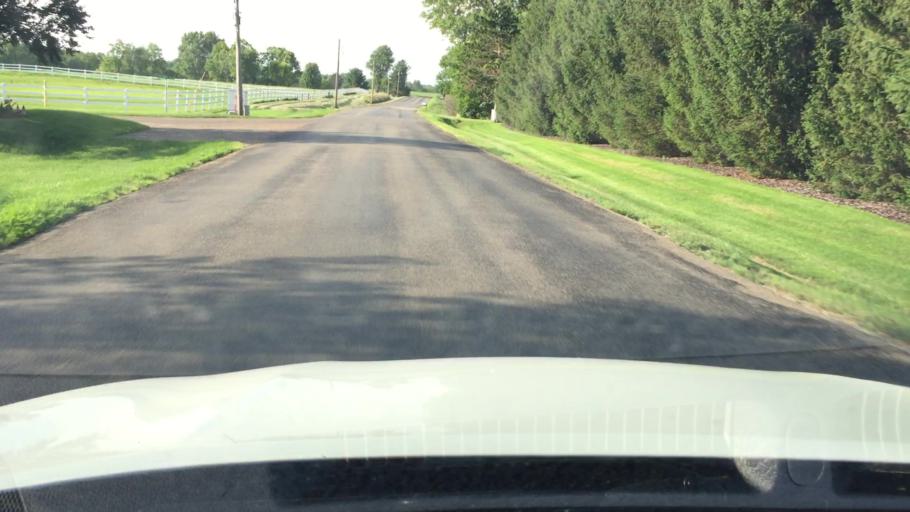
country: US
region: Iowa
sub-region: Johnson County
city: North Liberty
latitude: 41.8074
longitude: -91.6156
